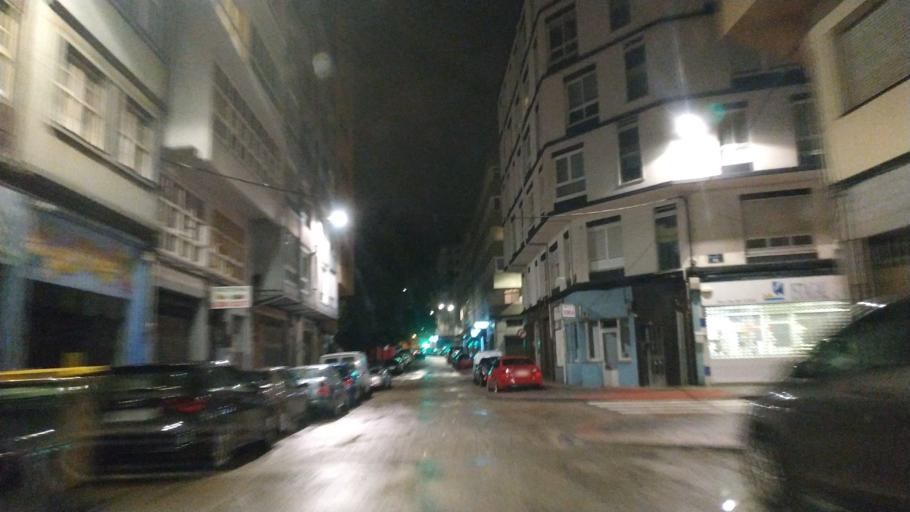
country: ES
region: Galicia
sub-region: Provincia da Coruna
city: A Coruna
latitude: 43.3579
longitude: -8.4148
